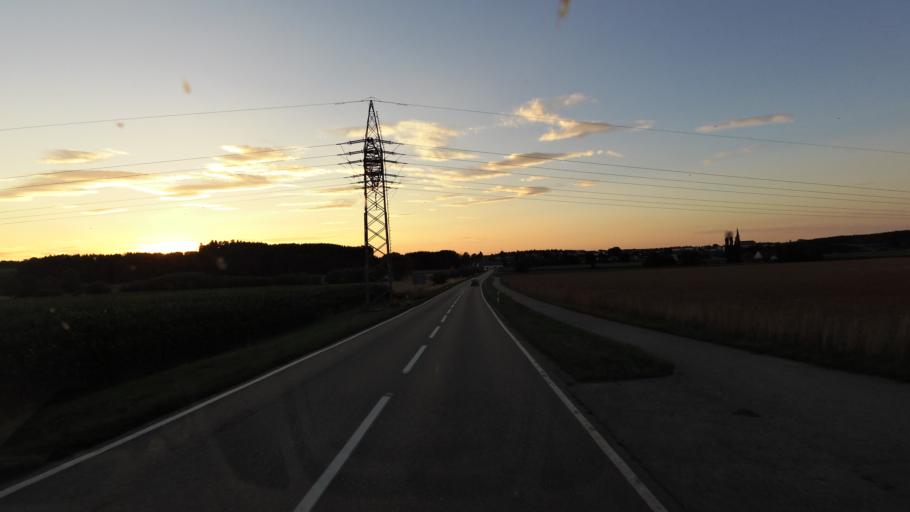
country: DE
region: Bavaria
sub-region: Upper Bavaria
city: Taufkirchen
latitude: 48.1381
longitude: 12.4549
